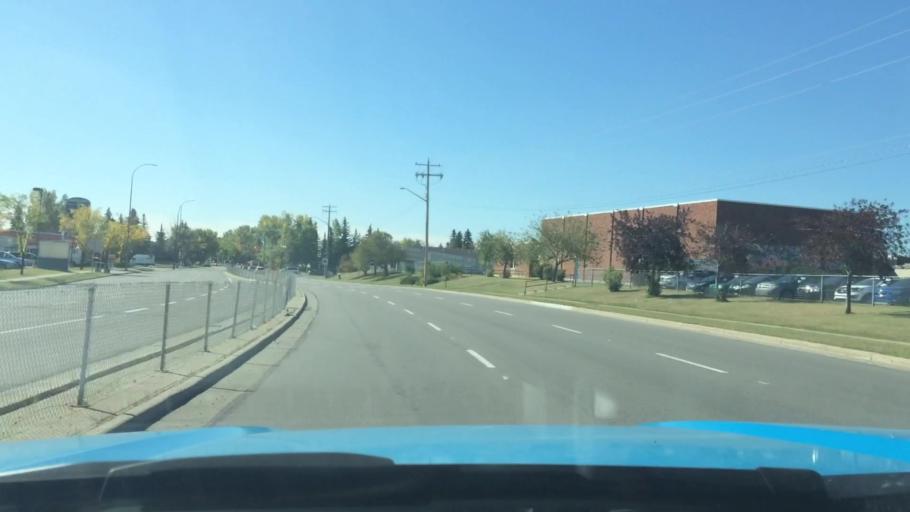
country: CA
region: Alberta
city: Calgary
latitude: 51.1124
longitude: -114.0568
